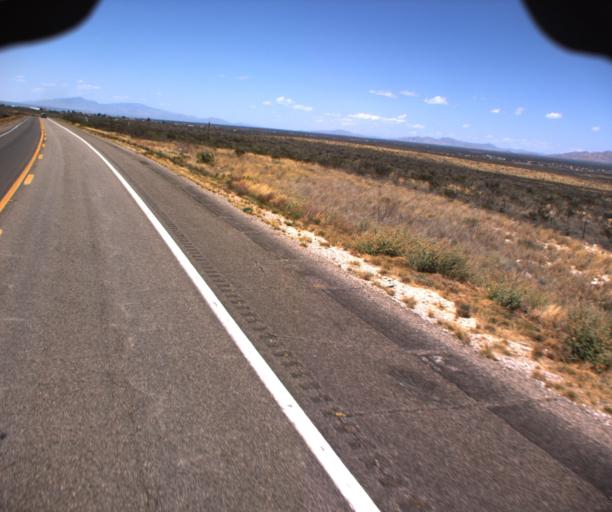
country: US
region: Arizona
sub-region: Cochise County
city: Tombstone
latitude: 31.6892
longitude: -110.0359
